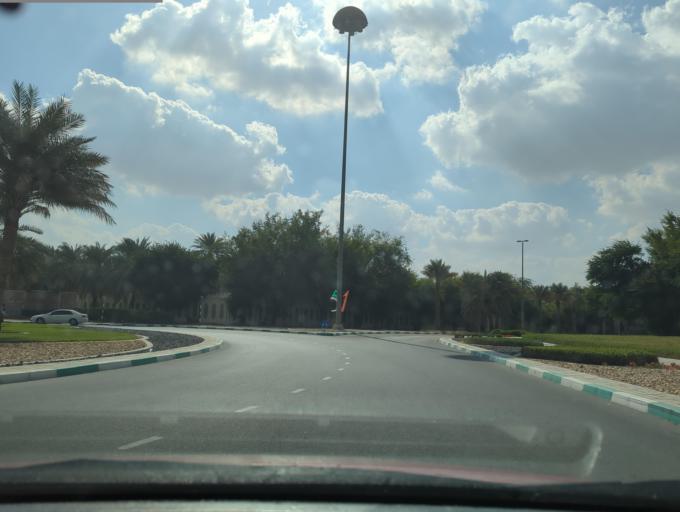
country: AE
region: Abu Dhabi
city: Al Ain
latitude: 24.1856
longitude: 55.6371
